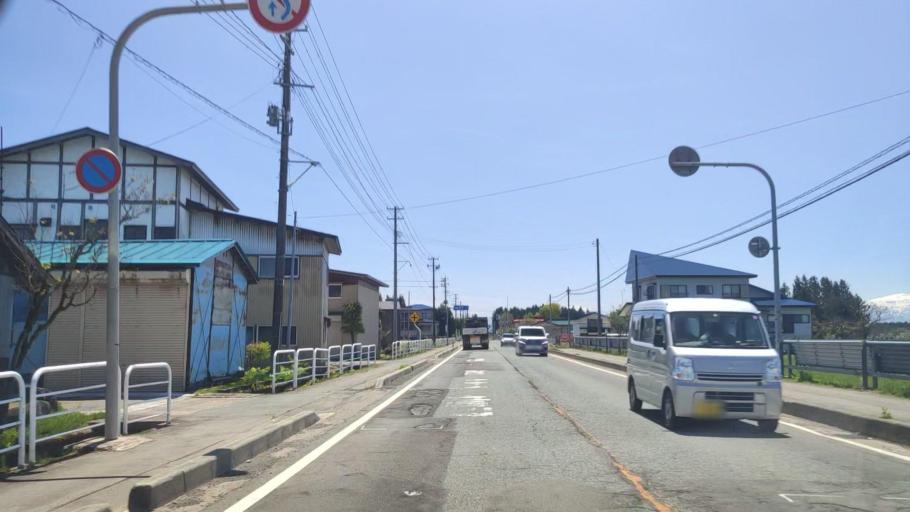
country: JP
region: Yamagata
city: Shinjo
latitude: 38.8282
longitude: 140.3277
